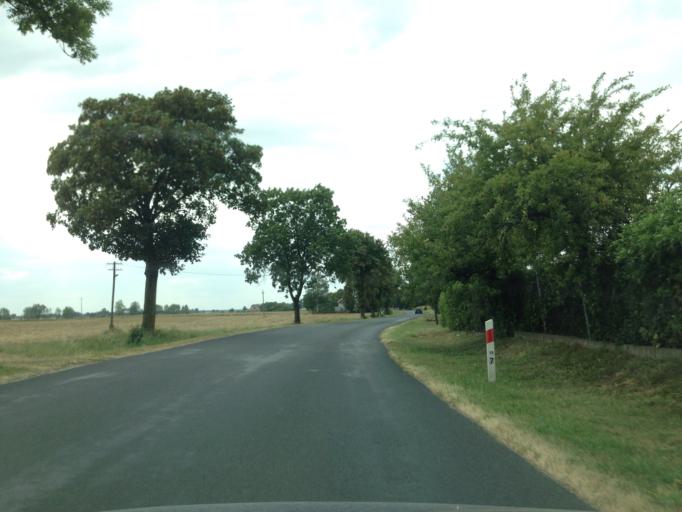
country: PL
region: Kujawsko-Pomorskie
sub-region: Powiat golubsko-dobrzynski
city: Kowalewo Pomorskie
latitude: 53.1723
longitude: 18.8380
